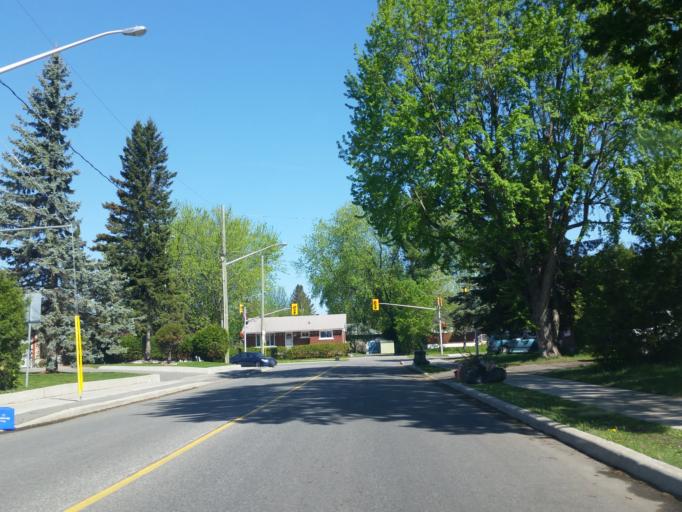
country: CA
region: Ontario
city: Ottawa
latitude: 45.3449
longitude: -75.7474
